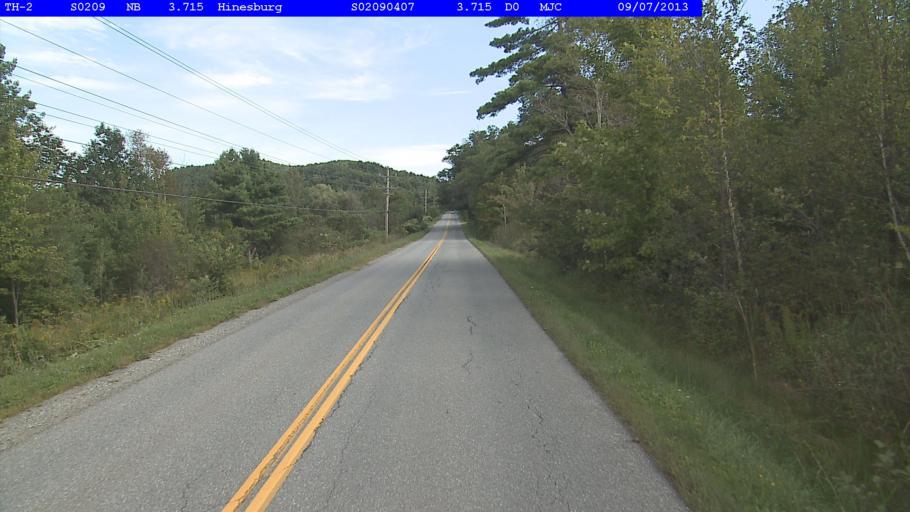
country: US
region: Vermont
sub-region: Chittenden County
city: Hinesburg
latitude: 44.3641
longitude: -73.0716
